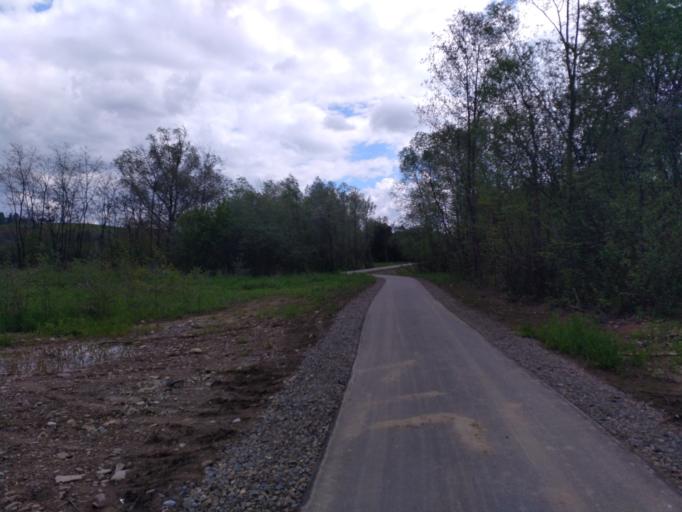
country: PL
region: Lesser Poland Voivodeship
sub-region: Powiat nowosadecki
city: Stary Sacz
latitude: 49.5801
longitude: 20.6473
